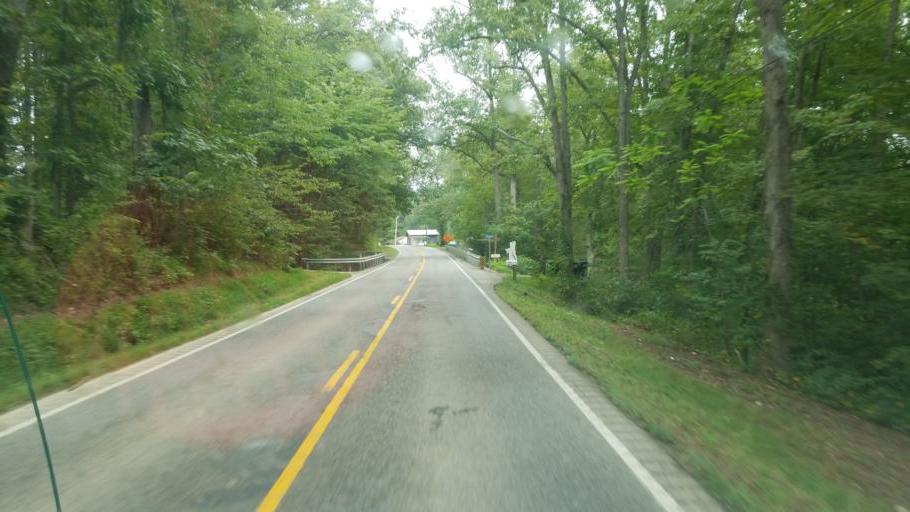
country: US
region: Kentucky
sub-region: Rowan County
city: Morehead
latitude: 38.2450
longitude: -83.4426
